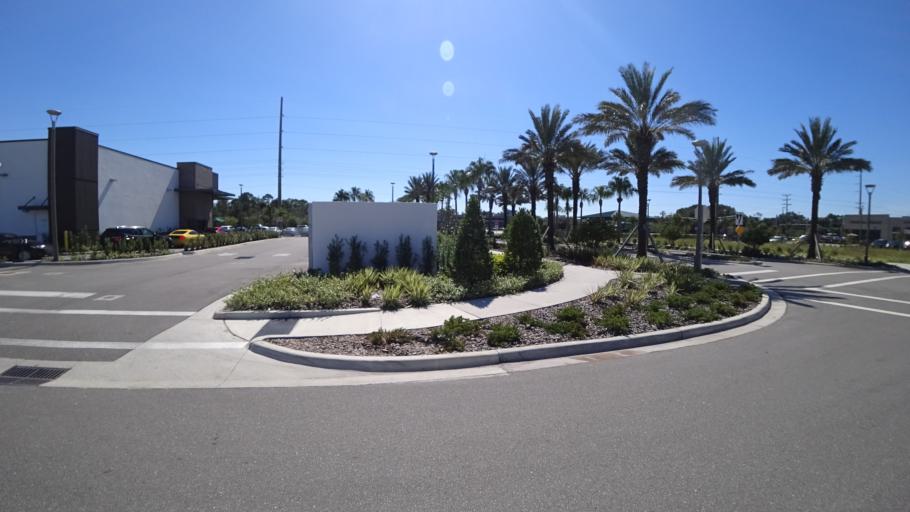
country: US
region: Florida
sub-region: Sarasota County
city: The Meadows
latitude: 27.4330
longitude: -82.4258
